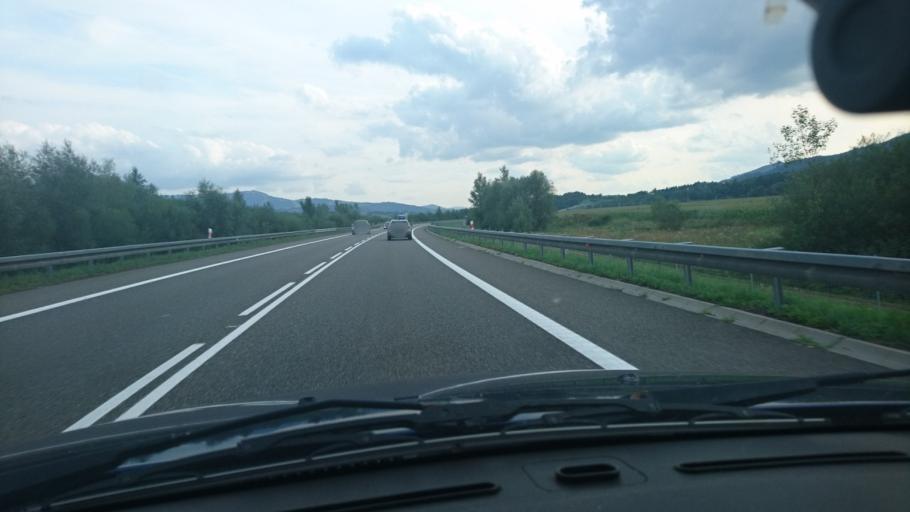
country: PL
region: Silesian Voivodeship
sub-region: Powiat zywiecki
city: Wieprz
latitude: 49.6388
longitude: 19.1665
